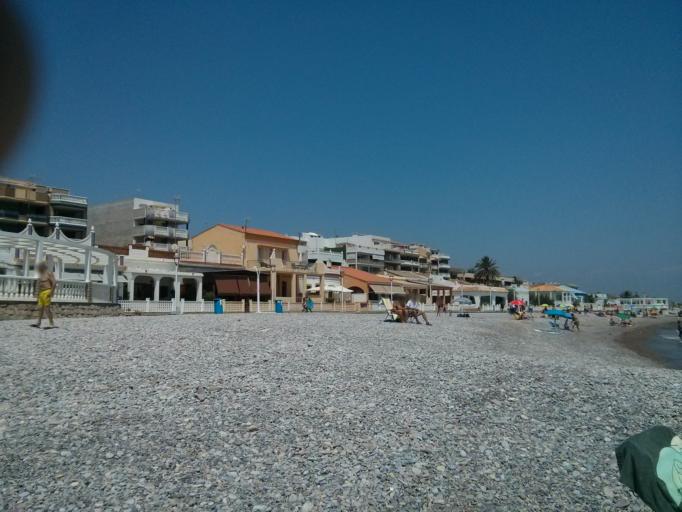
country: ES
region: Valencia
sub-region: Provincia de Castello
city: Moncofar
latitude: 39.8015
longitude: -0.1285
